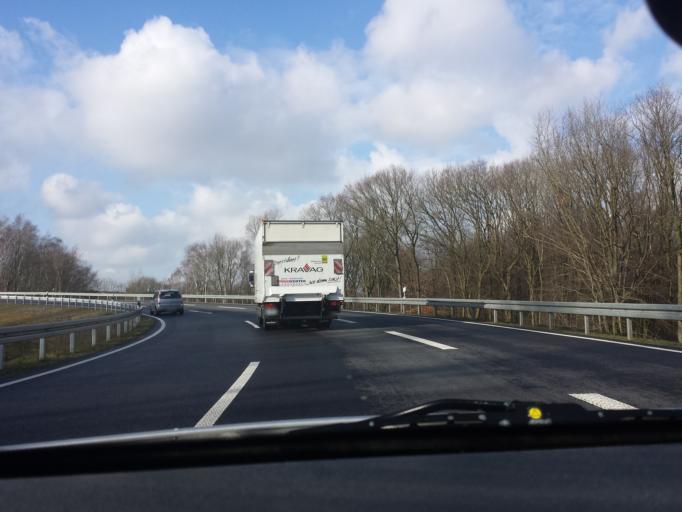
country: DE
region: North Rhine-Westphalia
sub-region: Regierungsbezirk Dusseldorf
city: Erkrath
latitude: 51.1913
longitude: 6.8708
